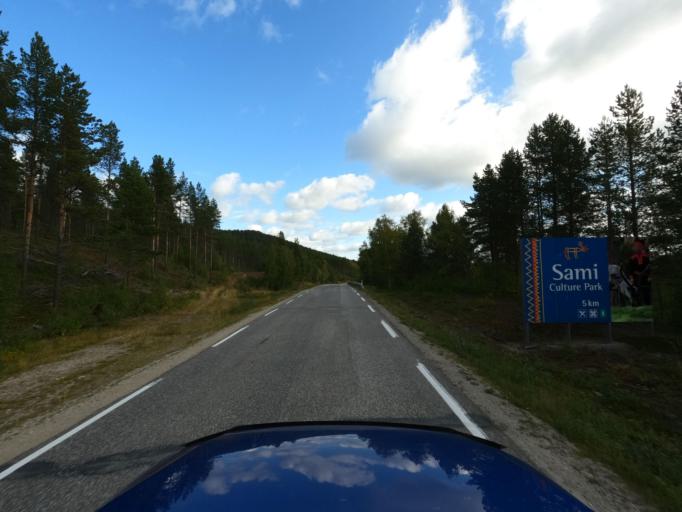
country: NO
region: Finnmark Fylke
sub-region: Karasjok
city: Karasjohka
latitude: 69.4562
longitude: 25.4007
